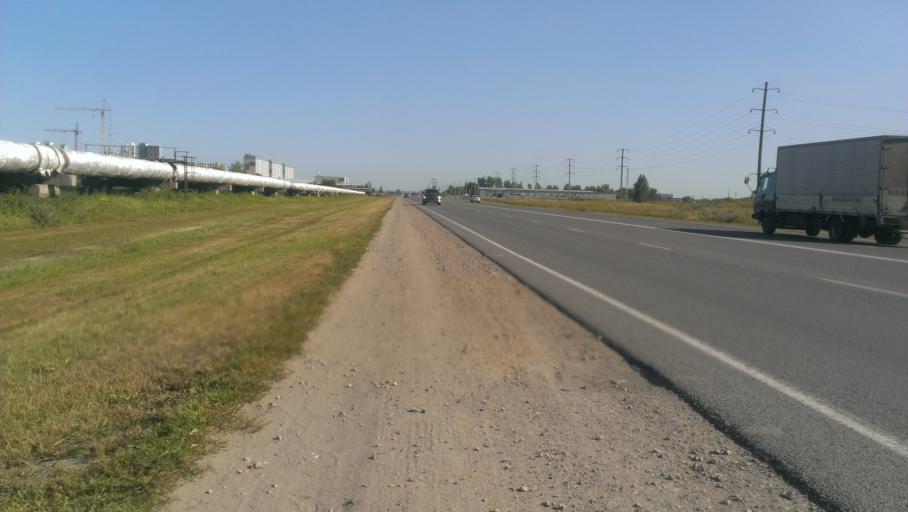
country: RU
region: Altai Krai
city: Novosilikatnyy
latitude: 53.3439
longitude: 83.6354
